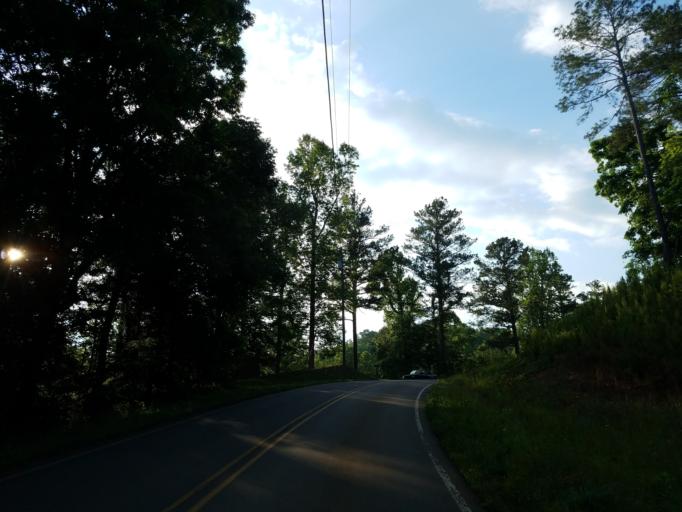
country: US
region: Georgia
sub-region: Cherokee County
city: Ball Ground
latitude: 34.3018
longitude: -84.3880
